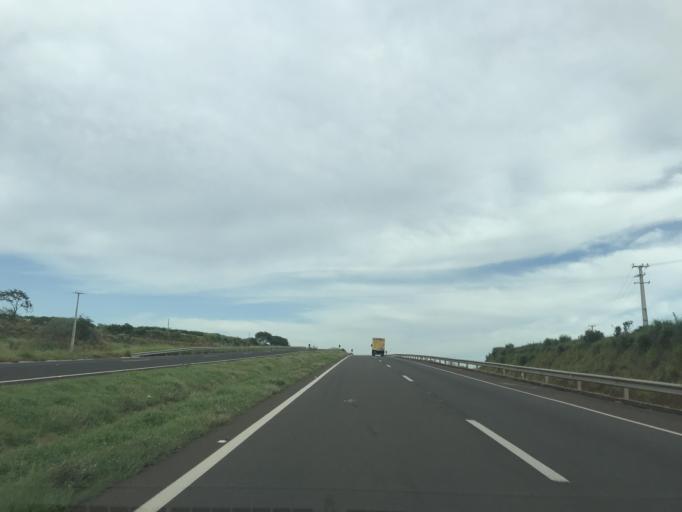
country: BR
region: Parana
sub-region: Alto Parana
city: Alto Parana
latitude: -23.1118
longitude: -52.3342
